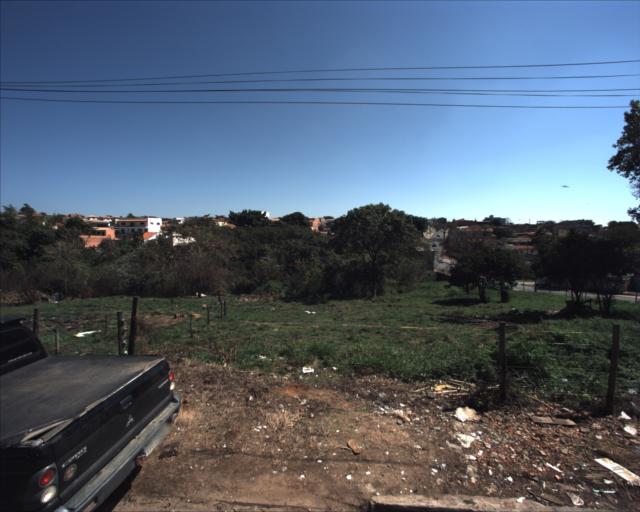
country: BR
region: Sao Paulo
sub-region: Sorocaba
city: Sorocaba
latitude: -23.4729
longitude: -47.4808
